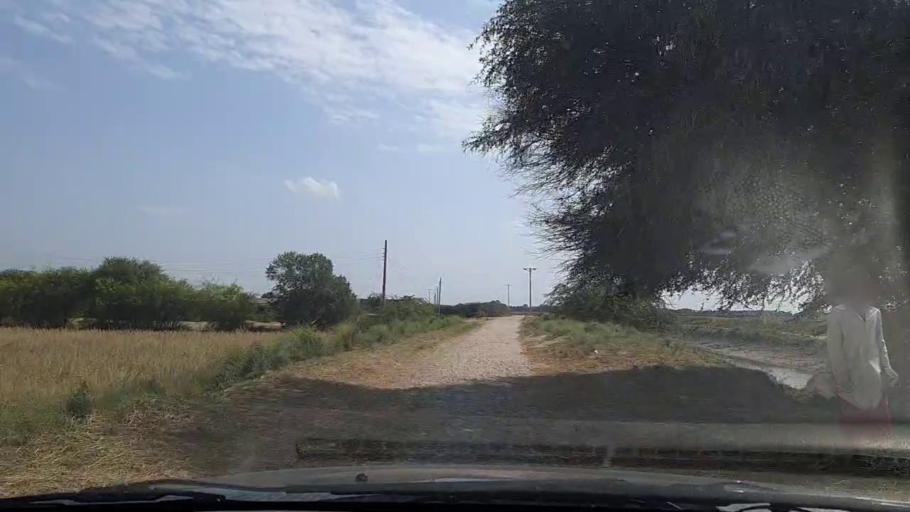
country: PK
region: Sindh
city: Mirpur Batoro
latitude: 24.5698
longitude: 68.1976
